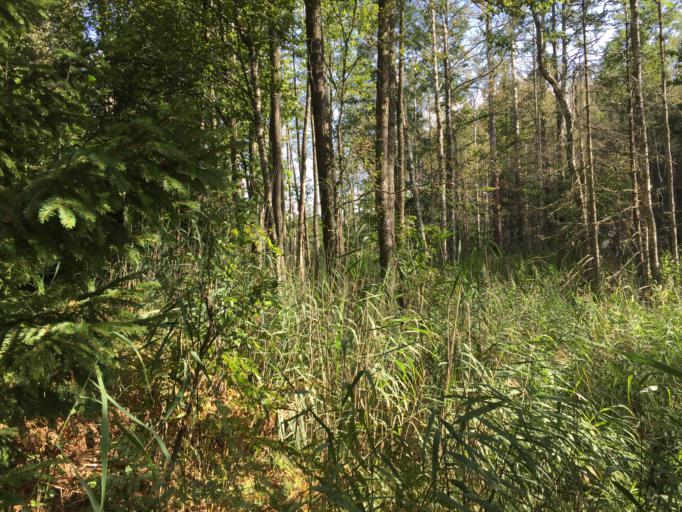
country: LV
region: Kuldigas Rajons
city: Kuldiga
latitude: 57.0033
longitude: 21.7922
